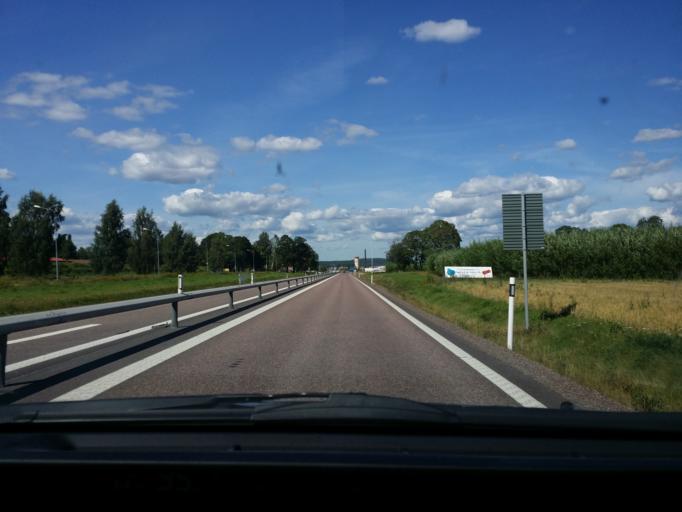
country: SE
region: Dalarna
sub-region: Hedemora Kommun
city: Hedemora
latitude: 60.2748
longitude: 16.0005
